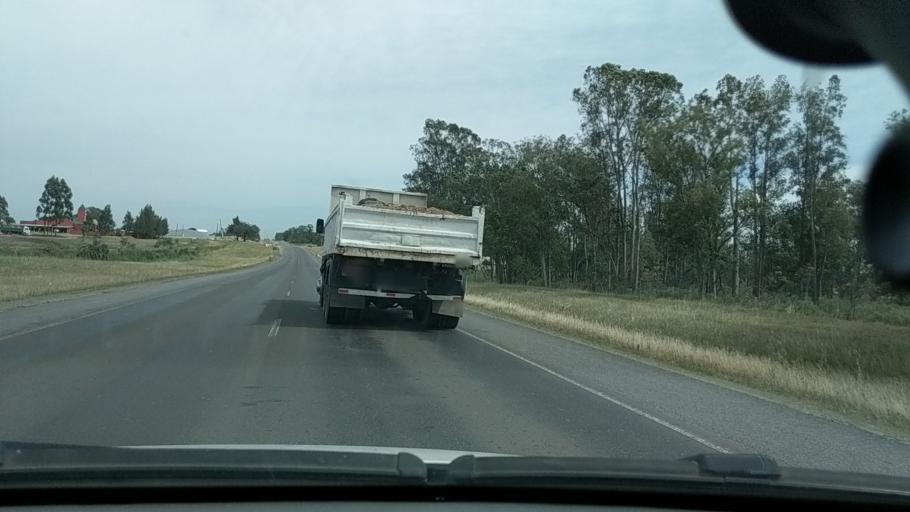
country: UY
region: Durazno
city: Durazno
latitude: -33.4258
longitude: -56.4990
